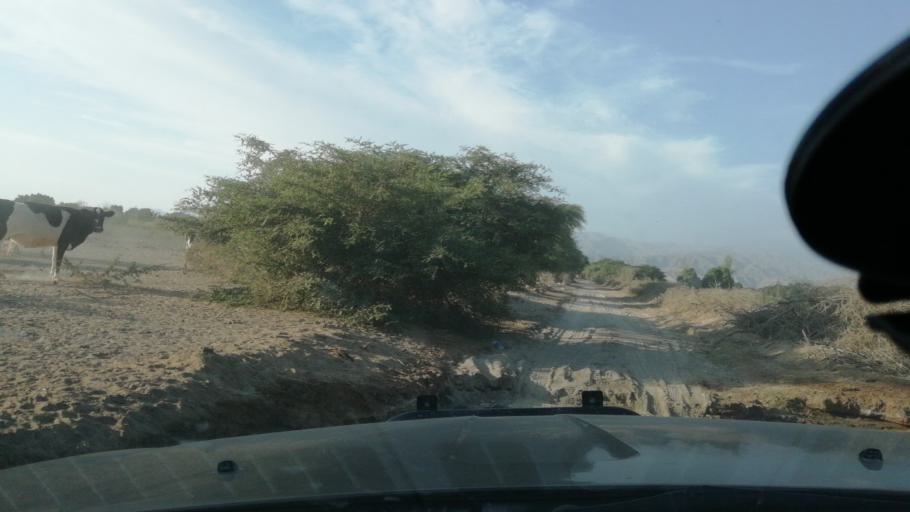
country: PE
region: Ica
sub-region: Provincia de Chincha
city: San Pedro
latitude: -13.3461
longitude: -76.1609
